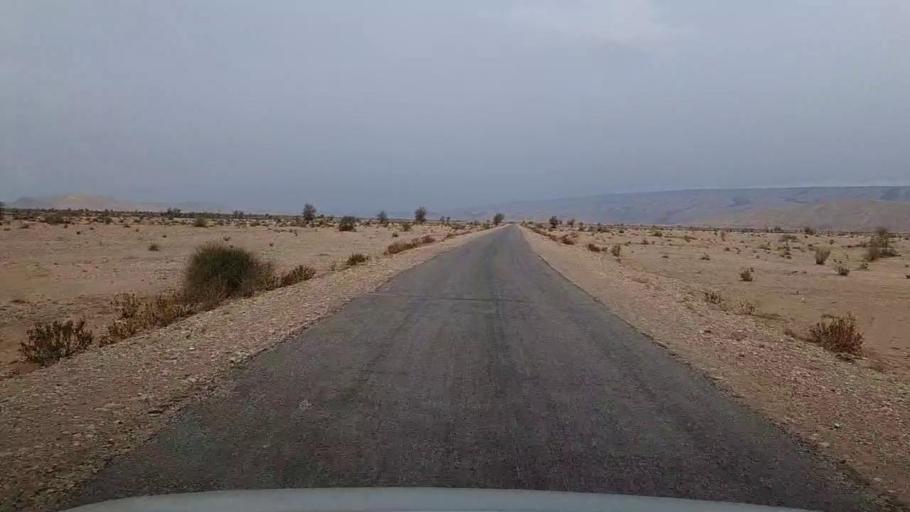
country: PK
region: Sindh
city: Sehwan
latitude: 26.2620
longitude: 67.7228
